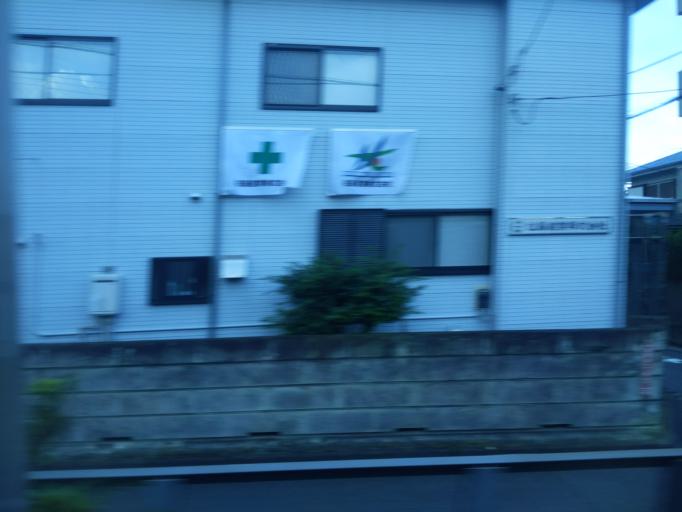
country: JP
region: Tokyo
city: Tokyo
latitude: 35.6794
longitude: 139.6332
